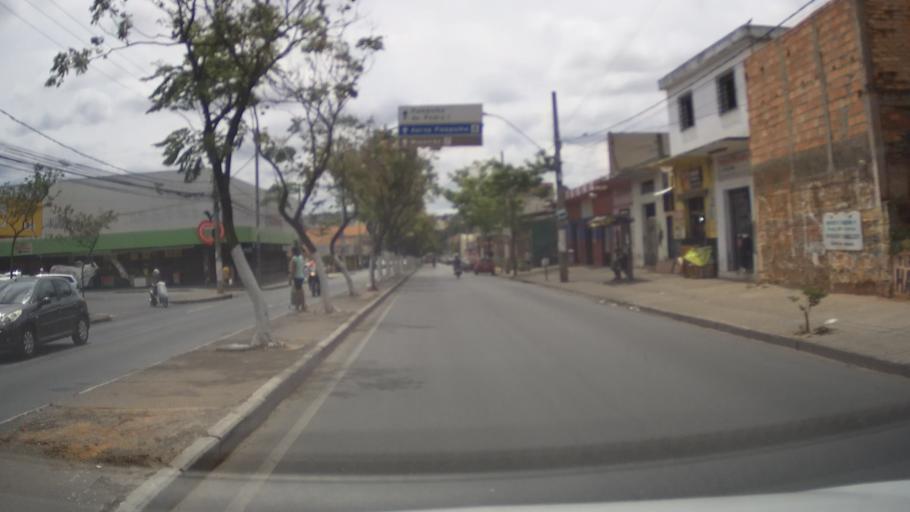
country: BR
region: Minas Gerais
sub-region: Ribeirao Das Neves
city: Ribeirao das Neves
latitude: -19.8039
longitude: -43.9788
